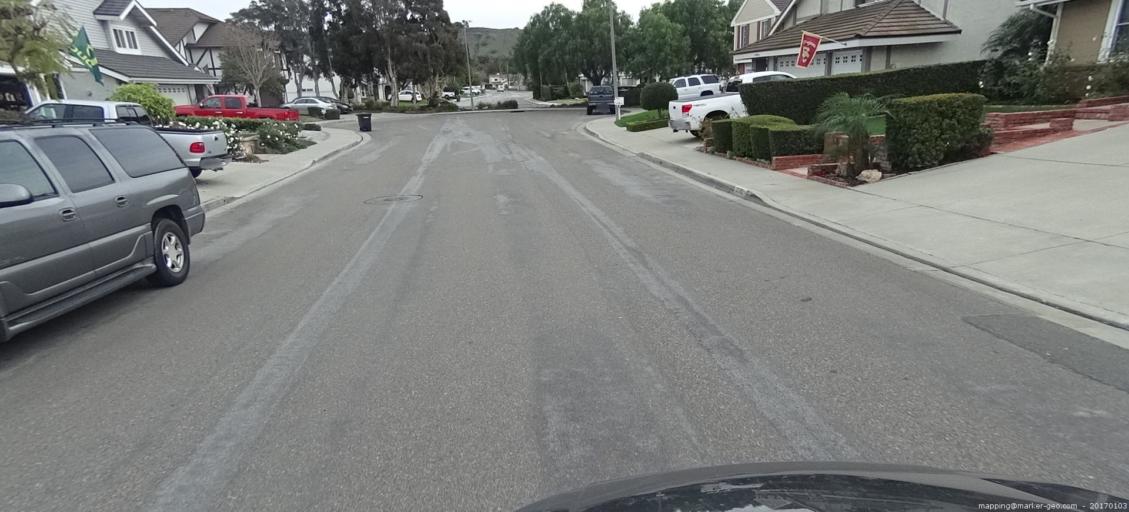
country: US
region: California
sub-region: Orange County
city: Dana Point
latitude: 33.4799
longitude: -117.6839
